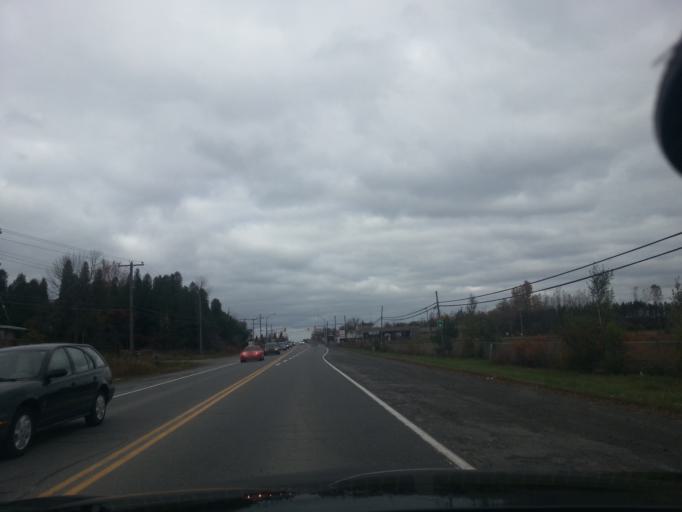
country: CA
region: Ontario
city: Ottawa
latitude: 45.2950
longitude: -75.5789
